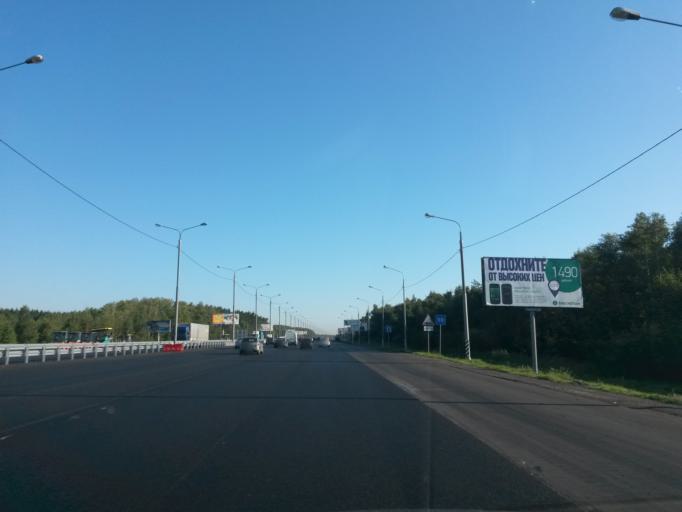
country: RU
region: Moskovskaya
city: Shcherbinka
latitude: 55.4866
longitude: 37.6132
